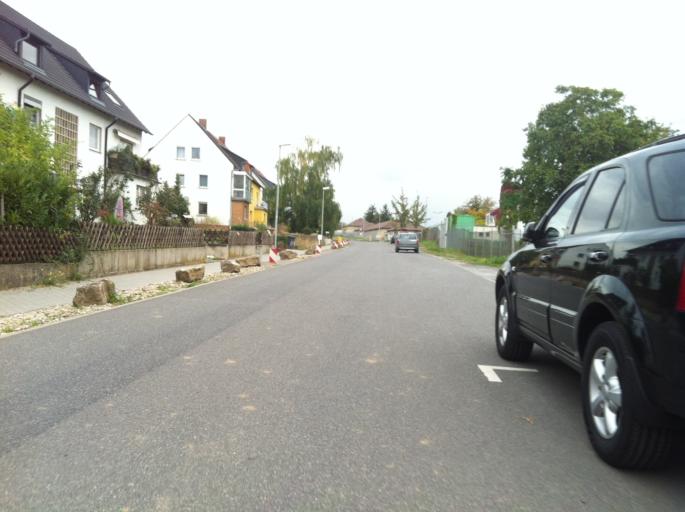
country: DE
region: Rheinland-Pfalz
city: Wackernheim
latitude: 49.9724
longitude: 8.1170
